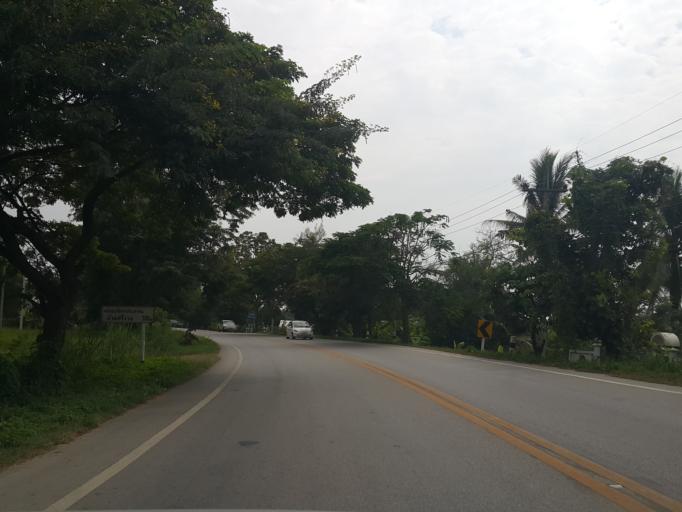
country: TH
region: Chiang Mai
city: Mae Taeng
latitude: 19.0321
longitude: 98.9667
